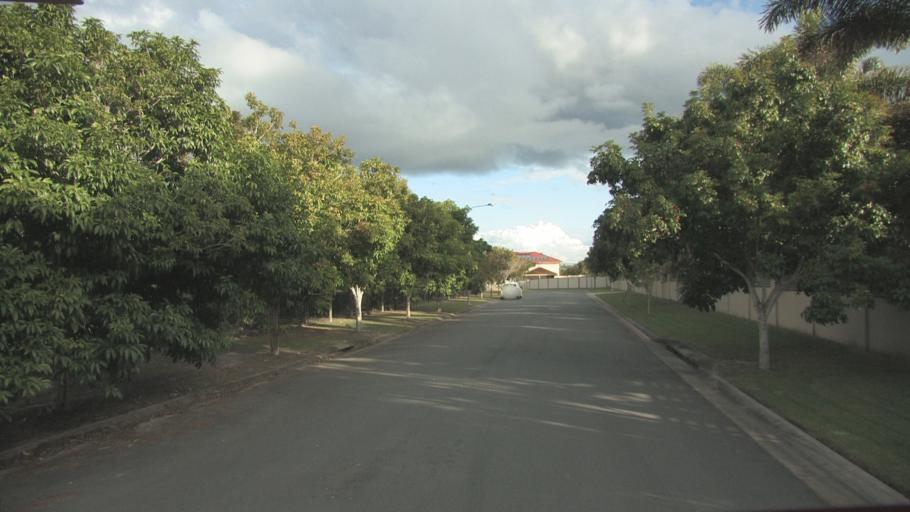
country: AU
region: Queensland
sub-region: Logan
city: Park Ridge South
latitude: -27.7053
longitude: 153.0221
